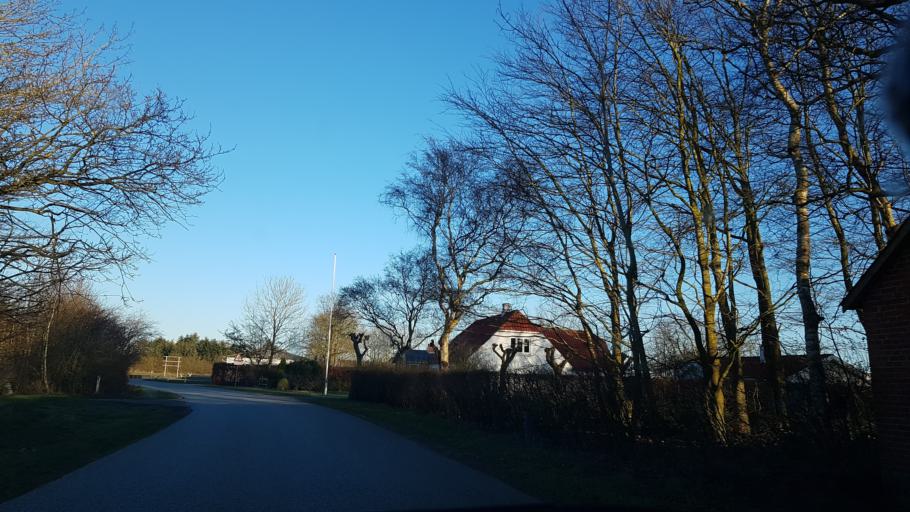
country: DK
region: South Denmark
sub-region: Esbjerg Kommune
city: Ribe
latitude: 55.3831
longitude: 8.7526
